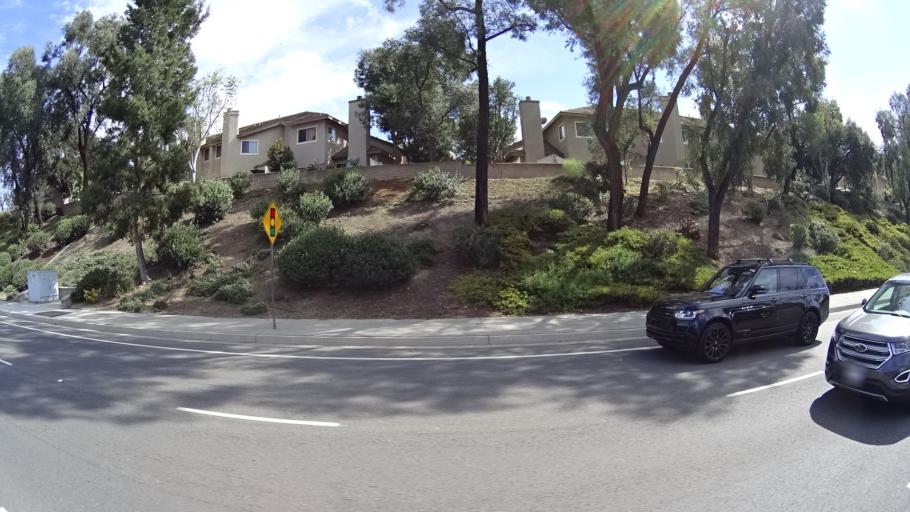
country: US
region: California
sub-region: Orange County
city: Laguna Hills
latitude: 33.5856
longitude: -117.7052
